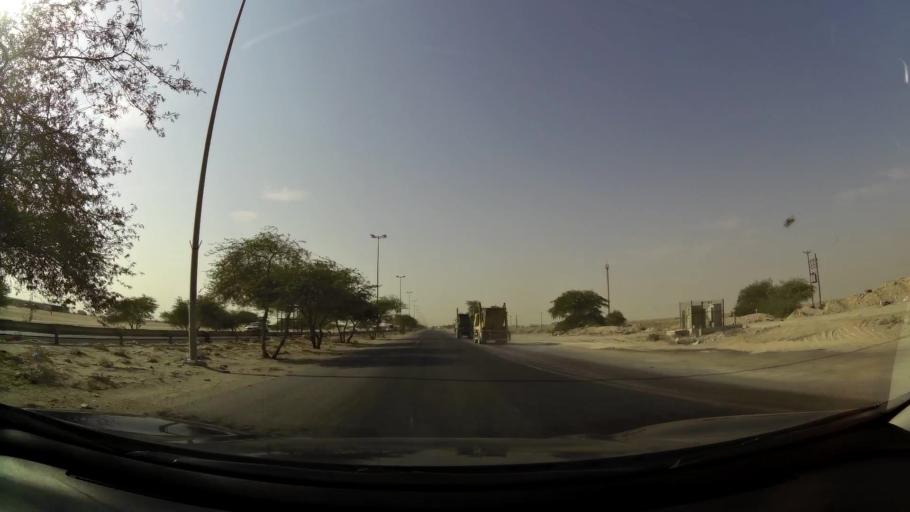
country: KW
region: Al Ahmadi
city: Al Ahmadi
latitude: 28.9380
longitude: 48.1108
